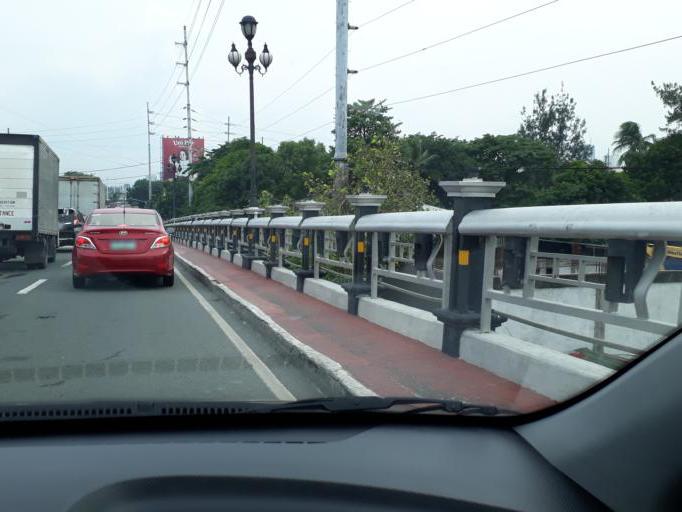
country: PH
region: Metro Manila
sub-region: City of Manila
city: Quiapo
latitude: 14.5950
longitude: 121.0015
